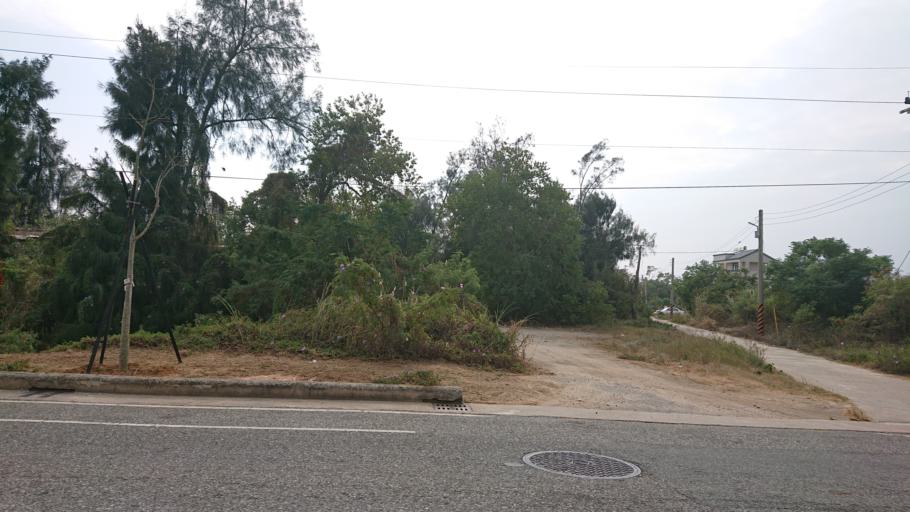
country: TW
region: Fukien
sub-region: Kinmen
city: Jincheng
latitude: 24.4567
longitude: 118.3767
